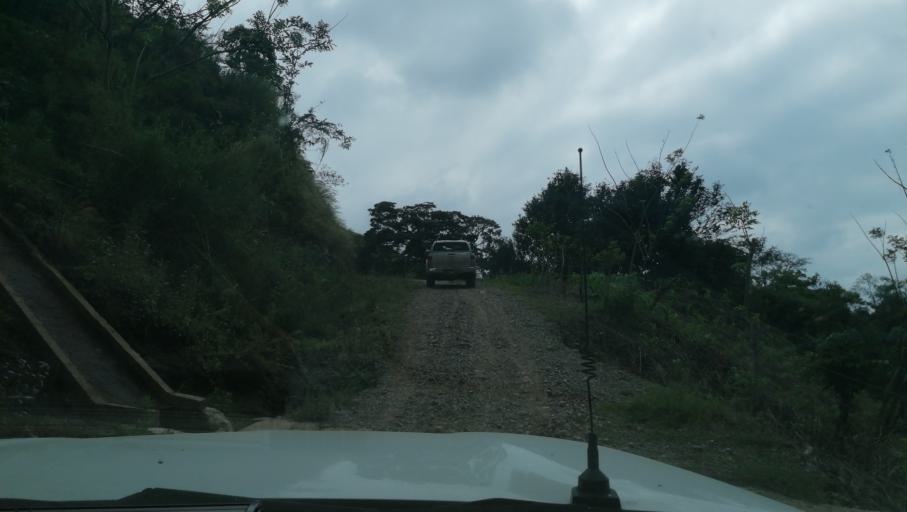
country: MX
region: Chiapas
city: Ostuacan
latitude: 17.3481
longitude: -93.3088
